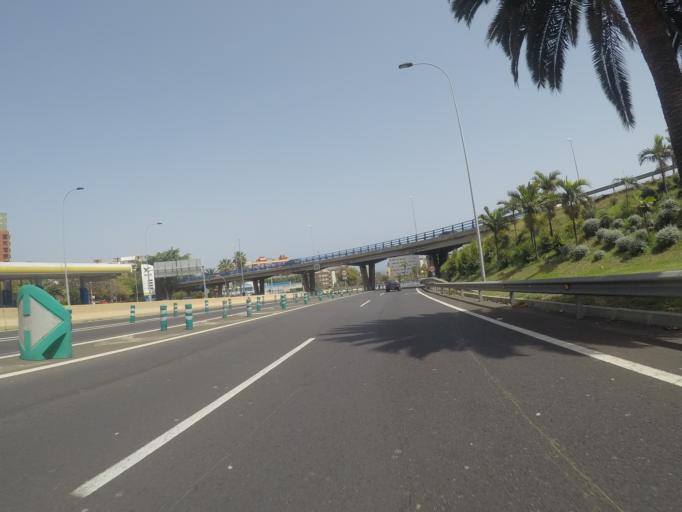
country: ES
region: Canary Islands
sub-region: Provincia de Santa Cruz de Tenerife
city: Santa Cruz de Tenerife
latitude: 28.4569
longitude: -16.2654
